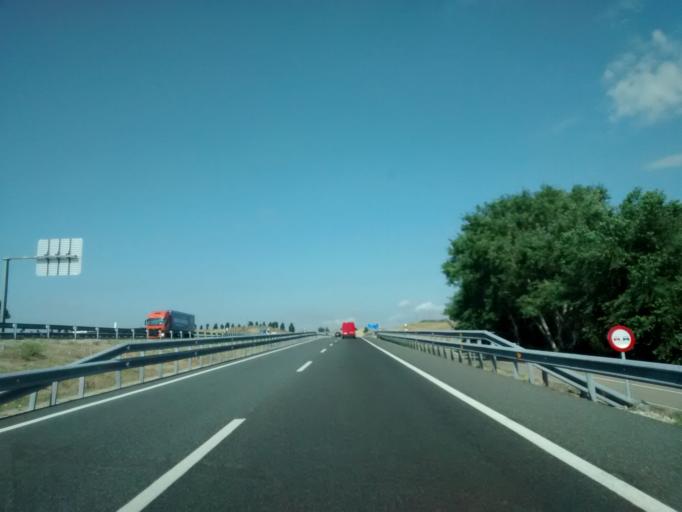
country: ES
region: Castille-La Mancha
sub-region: Province of Toledo
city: Otero
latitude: 40.0194
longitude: -4.5250
